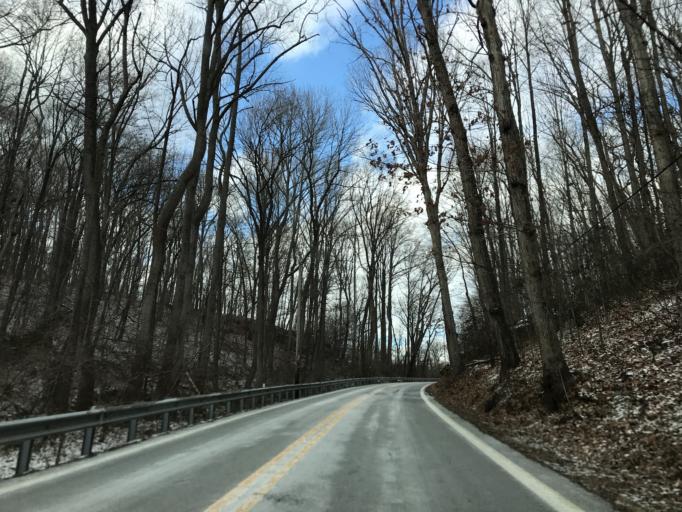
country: US
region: Maryland
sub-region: Harford County
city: Jarrettsville
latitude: 39.6476
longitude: -76.4101
